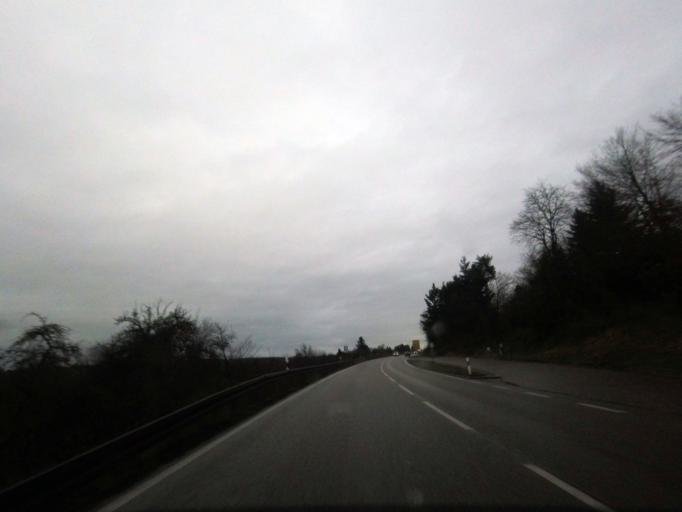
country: DE
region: Baden-Wuerttemberg
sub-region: Regierungsbezirk Stuttgart
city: Mittelschontal
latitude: 48.9510
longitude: 9.4123
